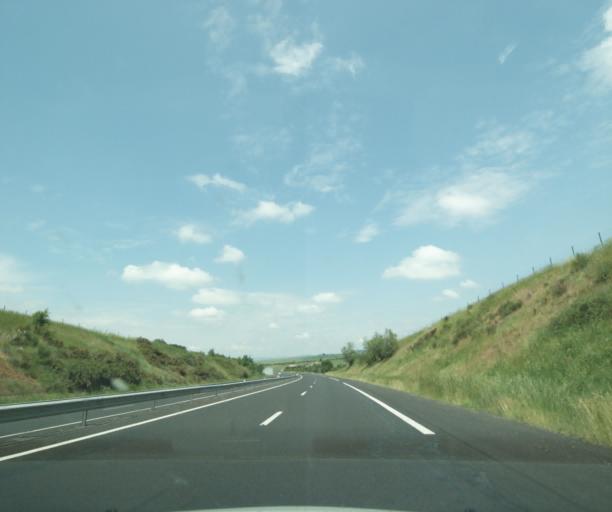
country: FR
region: Auvergne
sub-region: Departement de la Haute-Loire
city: Lempdes-sur-Allagnon
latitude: 45.3664
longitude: 3.2858
